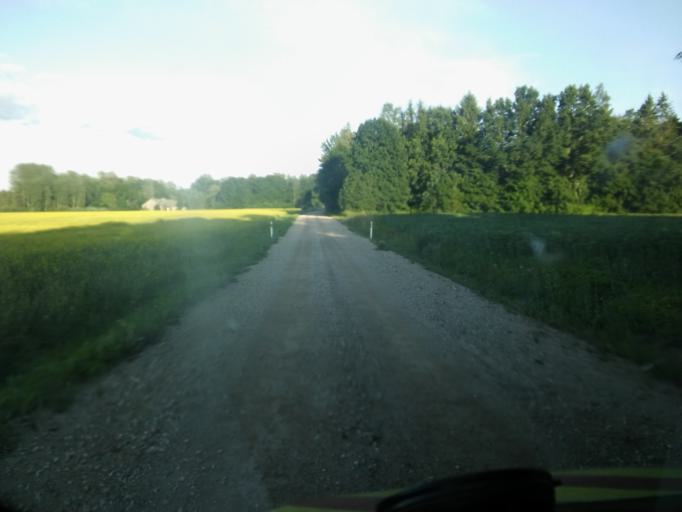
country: EE
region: Valgamaa
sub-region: Torva linn
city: Torva
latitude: 58.0583
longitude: 25.9160
